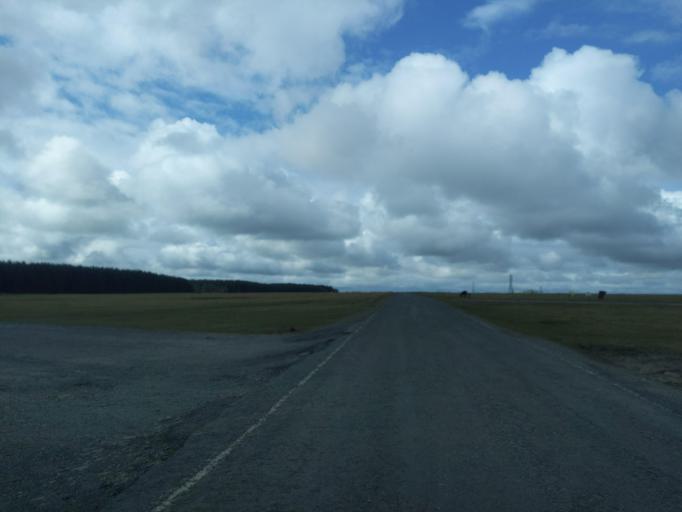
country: GB
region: England
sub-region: Cornwall
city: Camelford
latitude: 50.6327
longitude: -4.6111
